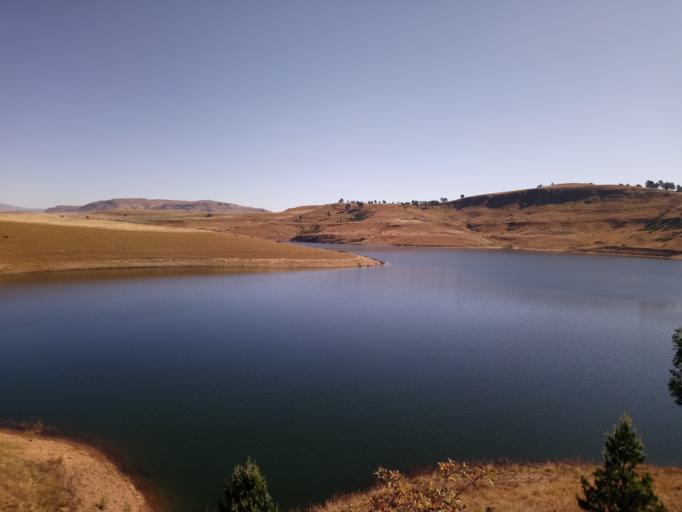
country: ZA
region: KwaZulu-Natal
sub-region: uMgungundlovu District Municipality
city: Mooirivier
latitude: -29.3337
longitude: 29.9181
